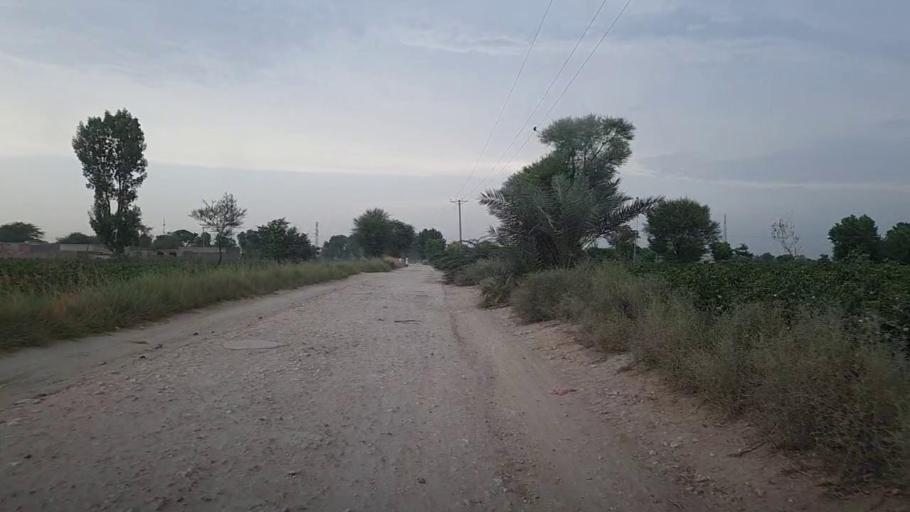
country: PK
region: Sindh
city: Karaundi
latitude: 26.9821
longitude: 68.3438
